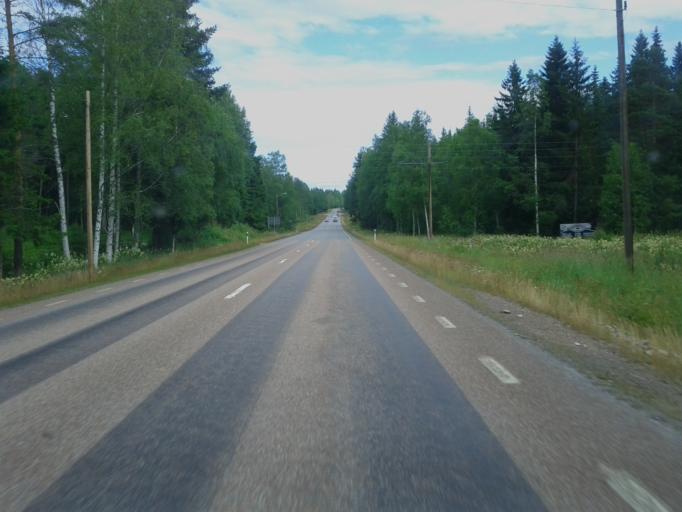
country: SE
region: Dalarna
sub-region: Faluns Kommun
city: Bjursas
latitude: 60.7409
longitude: 15.4118
